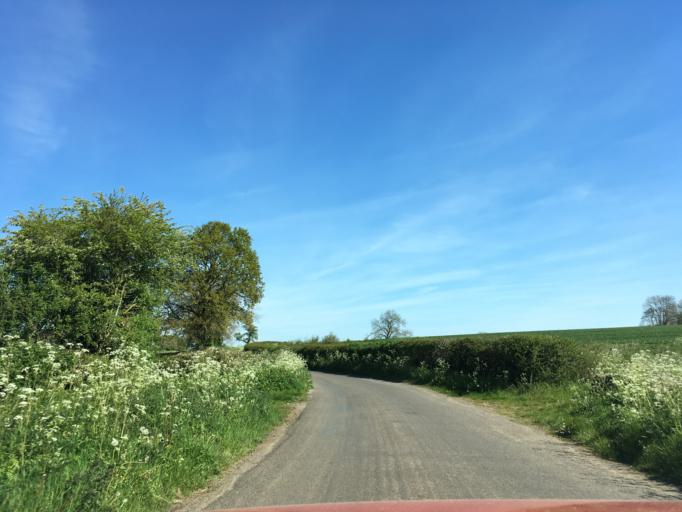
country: GB
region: England
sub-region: Wiltshire
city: Luckington
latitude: 51.5822
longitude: -2.2506
